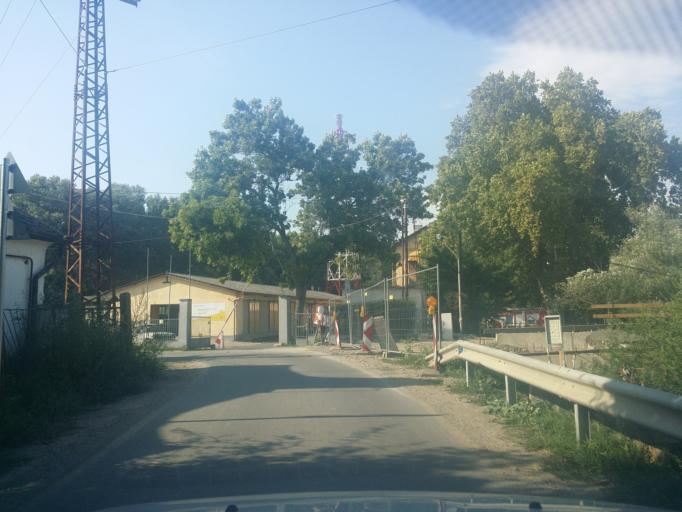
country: HU
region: Bacs-Kiskun
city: Baja
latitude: 46.1644
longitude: 18.9387
